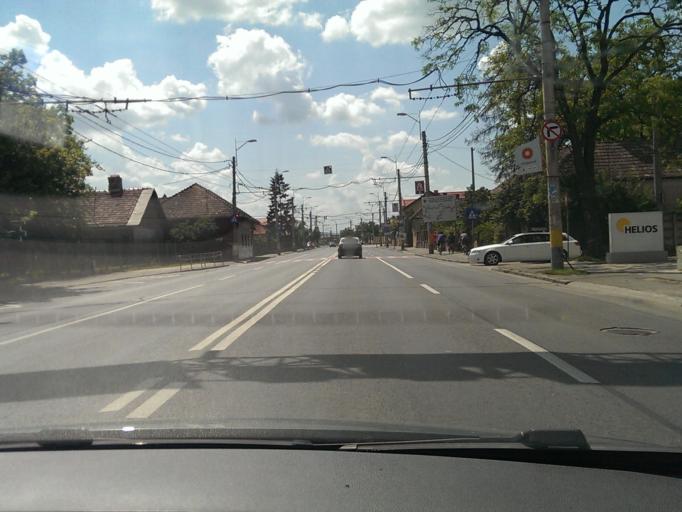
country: RO
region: Cluj
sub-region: Municipiul Cluj-Napoca
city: Cluj-Napoca
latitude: 46.7842
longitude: 23.6482
